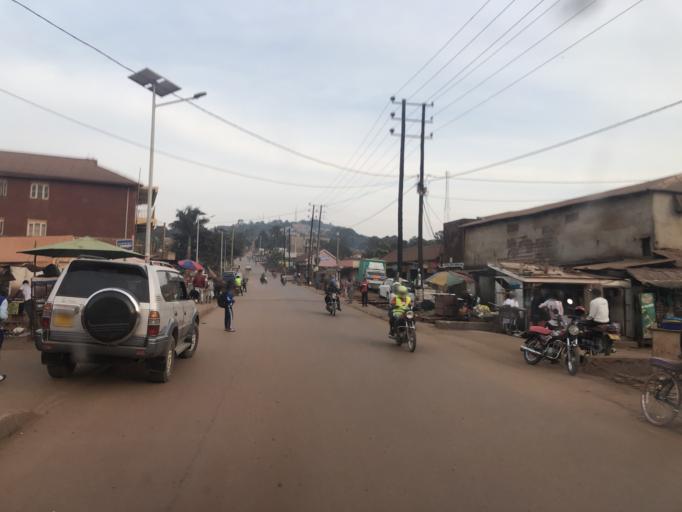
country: UG
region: Central Region
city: Kampala Central Division
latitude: 0.2963
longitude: 32.5270
